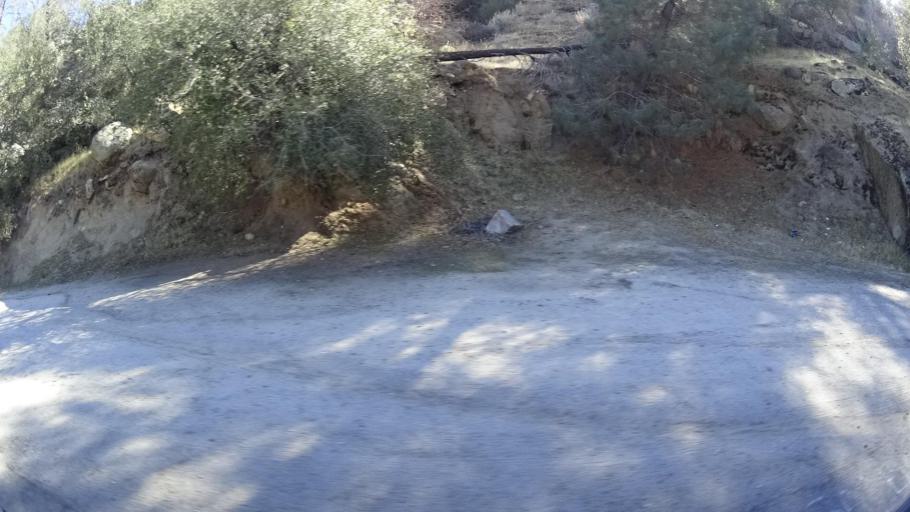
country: US
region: California
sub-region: Kern County
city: Bodfish
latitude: 35.5755
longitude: -118.5570
